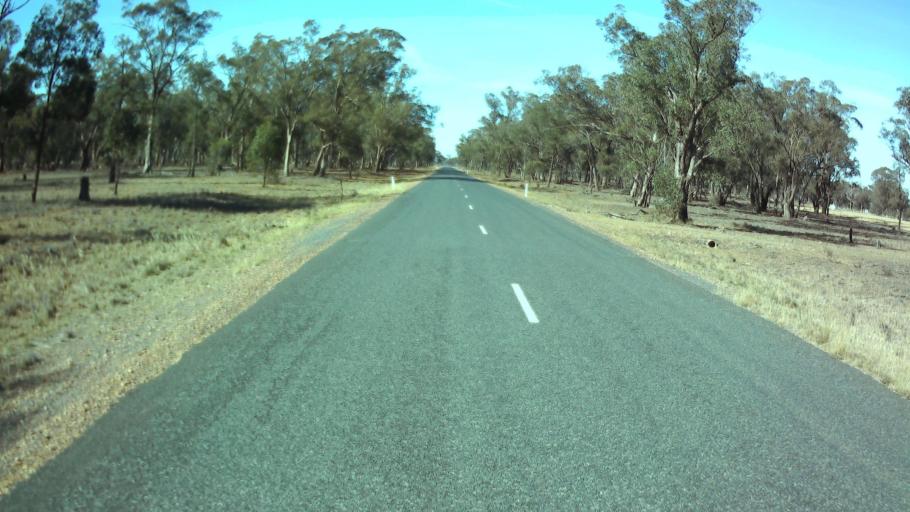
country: AU
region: New South Wales
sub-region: Weddin
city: Grenfell
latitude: -34.0622
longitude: 147.9091
